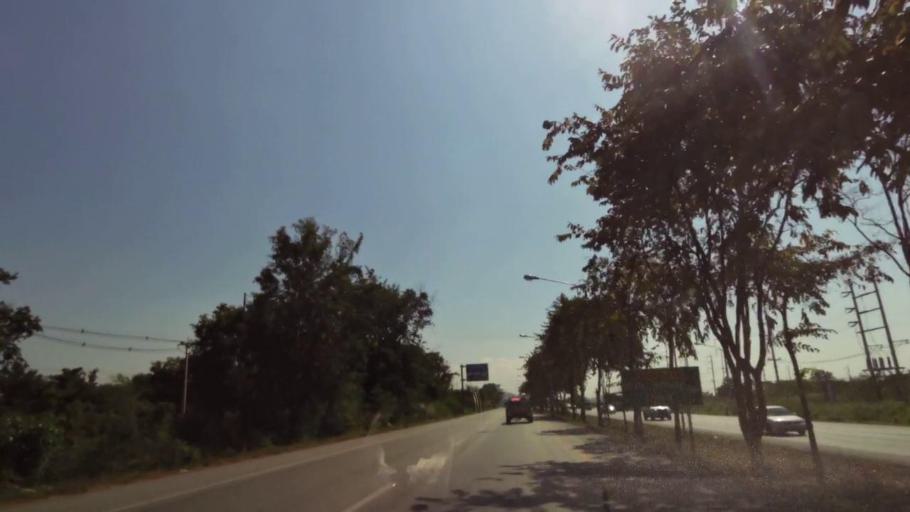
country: TH
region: Nakhon Sawan
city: Nakhon Sawan
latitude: 15.7718
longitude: 100.1213
